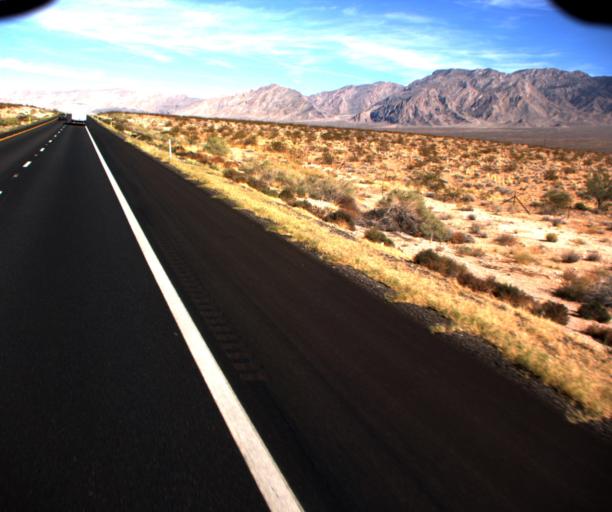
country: US
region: Arizona
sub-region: Mohave County
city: Beaver Dam
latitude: 36.8694
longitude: -113.9640
